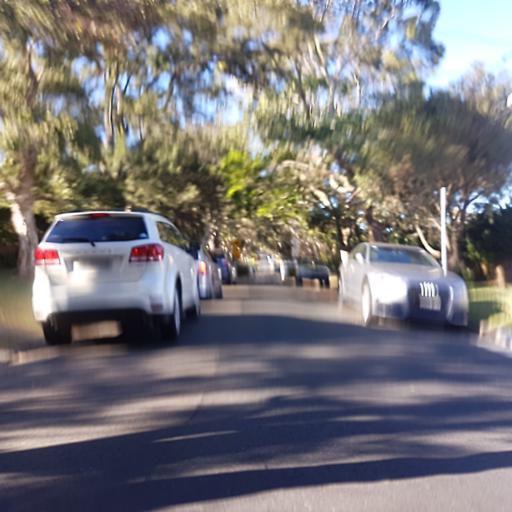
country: AU
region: New South Wales
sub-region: North Sydney
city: St Leonards
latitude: -33.8065
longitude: 151.2031
